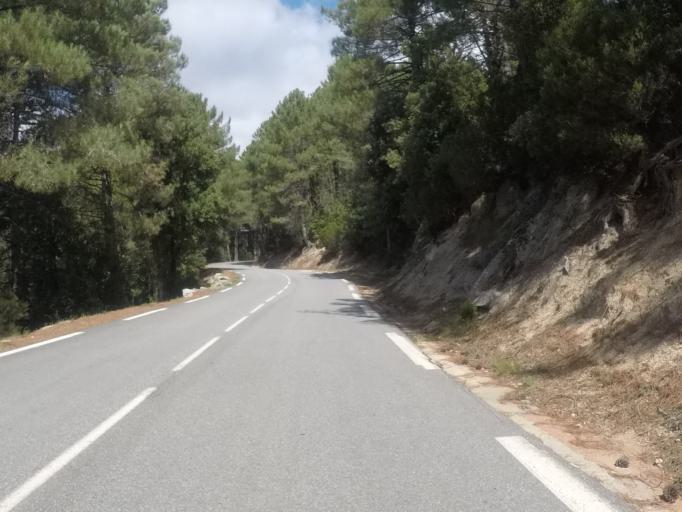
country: FR
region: Corsica
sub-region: Departement de la Corse-du-Sud
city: Zonza
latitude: 41.7653
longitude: 9.2071
